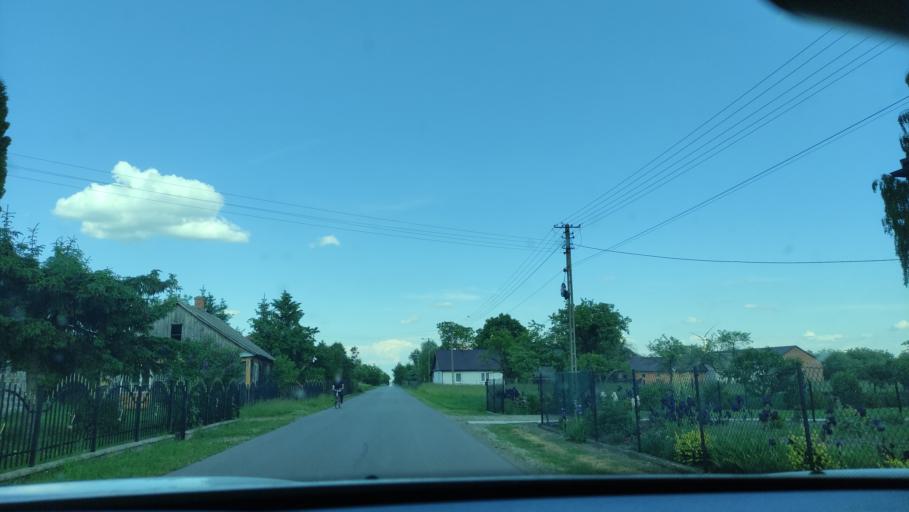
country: PL
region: Lublin Voivodeship
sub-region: Powiat lubartowski
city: Michow
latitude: 51.4966
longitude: 22.2822
